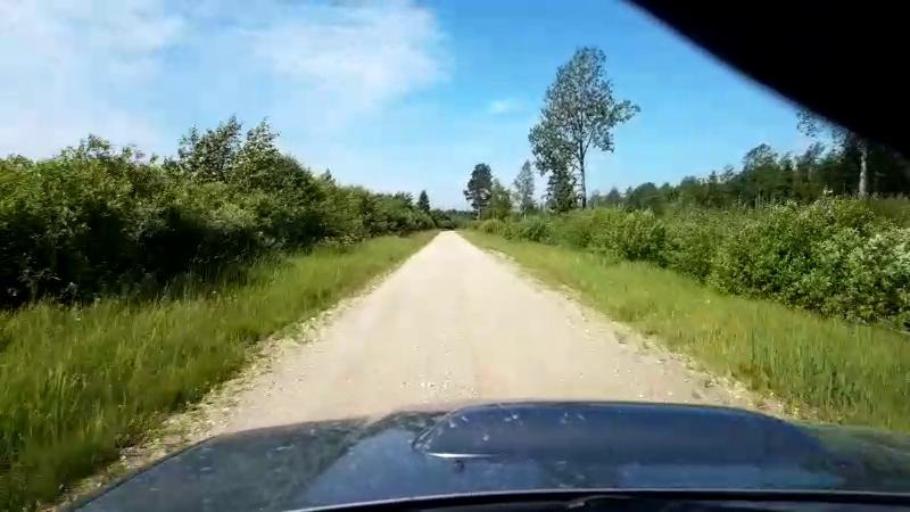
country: EE
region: Paernumaa
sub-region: Sindi linn
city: Sindi
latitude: 58.5108
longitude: 24.6796
